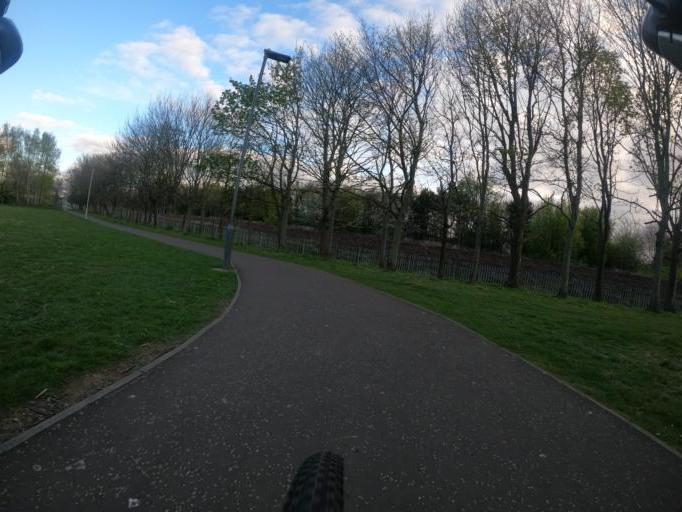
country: GB
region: Scotland
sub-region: Edinburgh
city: Currie
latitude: 55.9384
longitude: -3.3065
